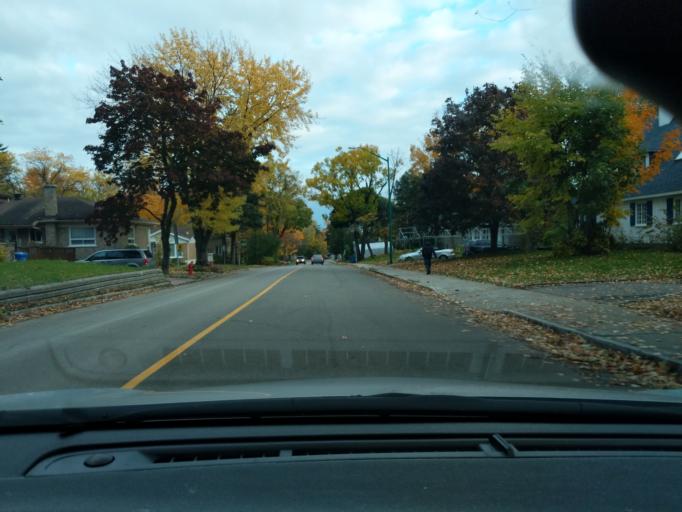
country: CA
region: Quebec
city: L'Ancienne-Lorette
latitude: 46.7609
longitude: -71.2895
